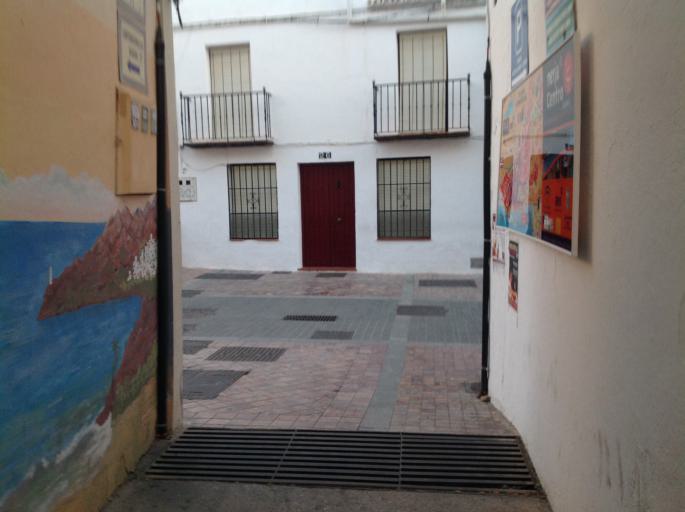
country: ES
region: Andalusia
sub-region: Provincia de Malaga
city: Nerja
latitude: 36.7462
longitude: -3.8747
